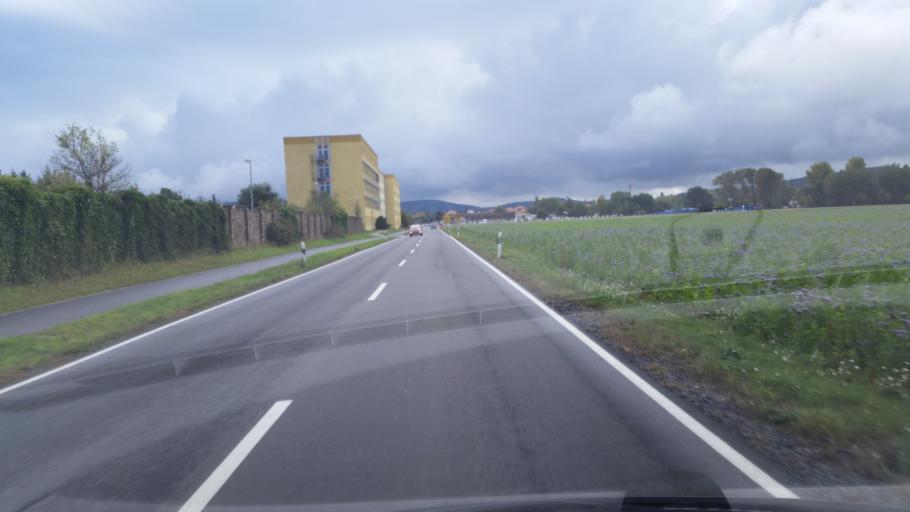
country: DE
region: Saxony
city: Kamenz
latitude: 51.2945
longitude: 14.1149
